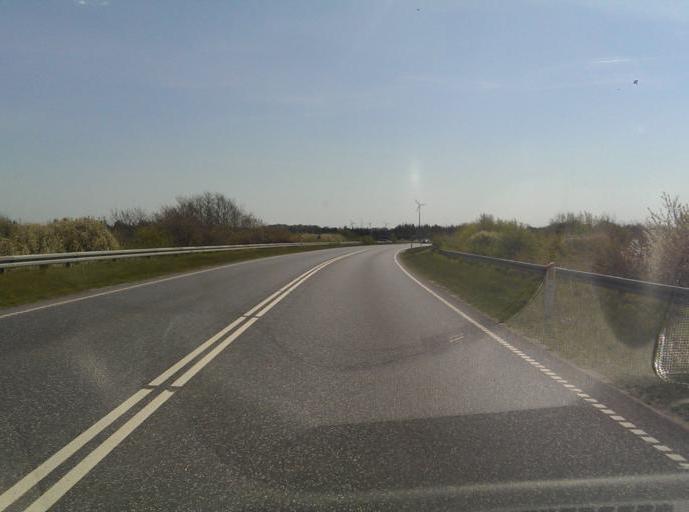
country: DK
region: South Denmark
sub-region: Esbjerg Kommune
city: Ribe
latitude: 55.3879
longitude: 8.7493
